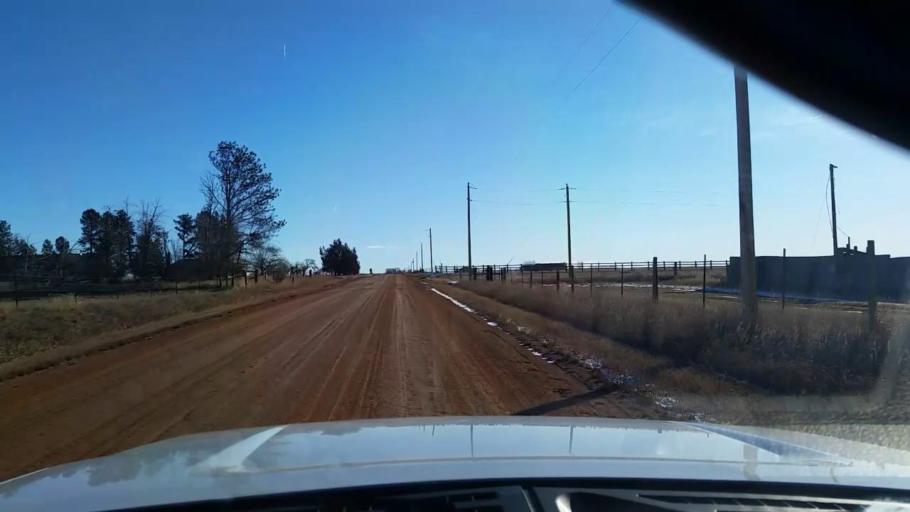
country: US
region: Colorado
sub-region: Larimer County
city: Wellington
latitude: 40.7694
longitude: -105.0675
